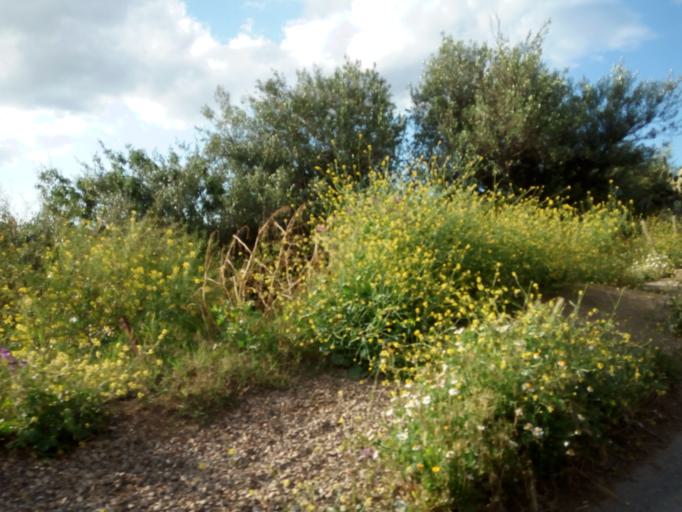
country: DZ
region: Tipaza
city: Hadjout
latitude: 36.3728
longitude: 2.4802
